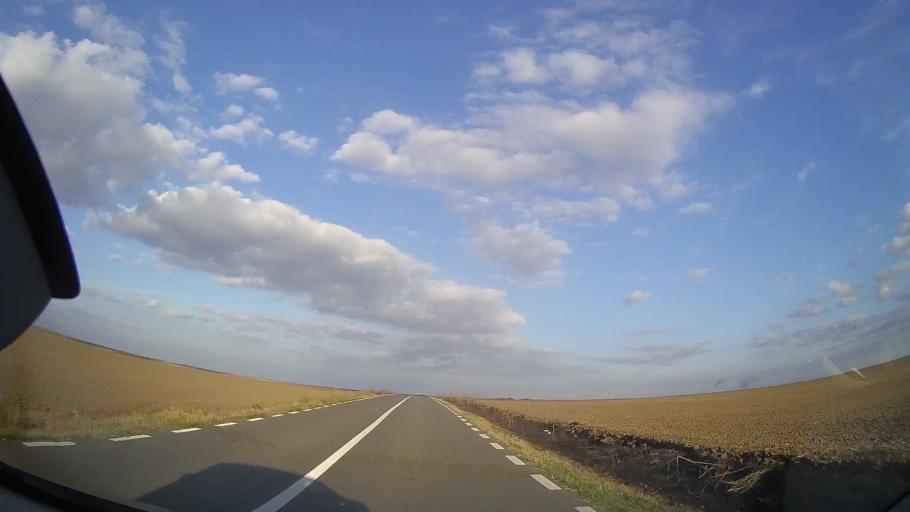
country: RO
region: Constanta
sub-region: Comuna Independenta
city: Independenta
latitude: 43.9435
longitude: 28.0568
